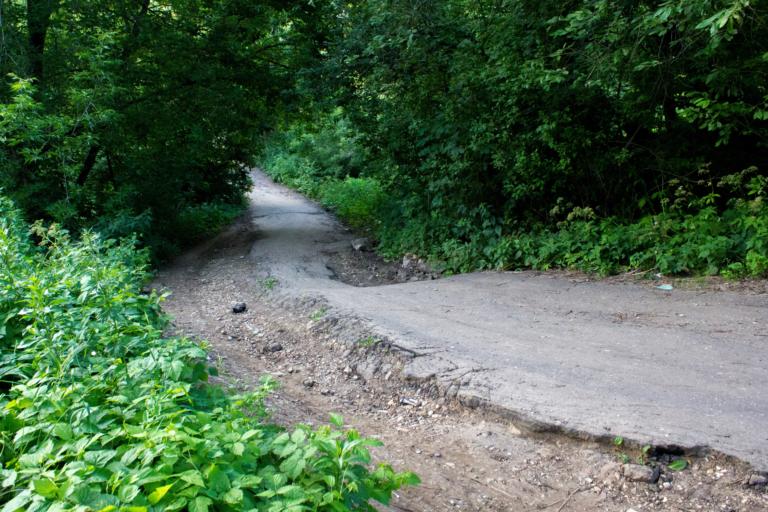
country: RU
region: Nizjnij Novgorod
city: Nizhniy Novgorod
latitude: 56.3242
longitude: 44.0417
